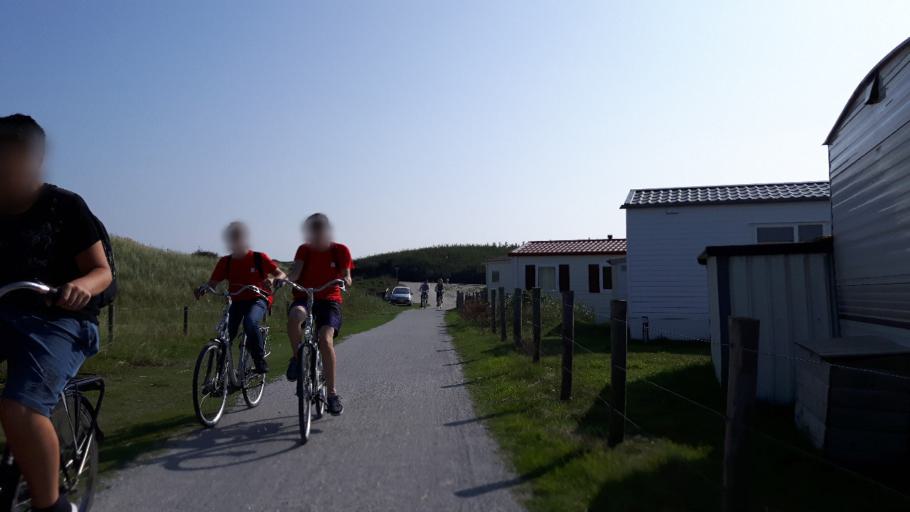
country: NL
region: Friesland
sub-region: Gemeente Ameland
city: Nes
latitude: 53.4586
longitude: 5.7758
